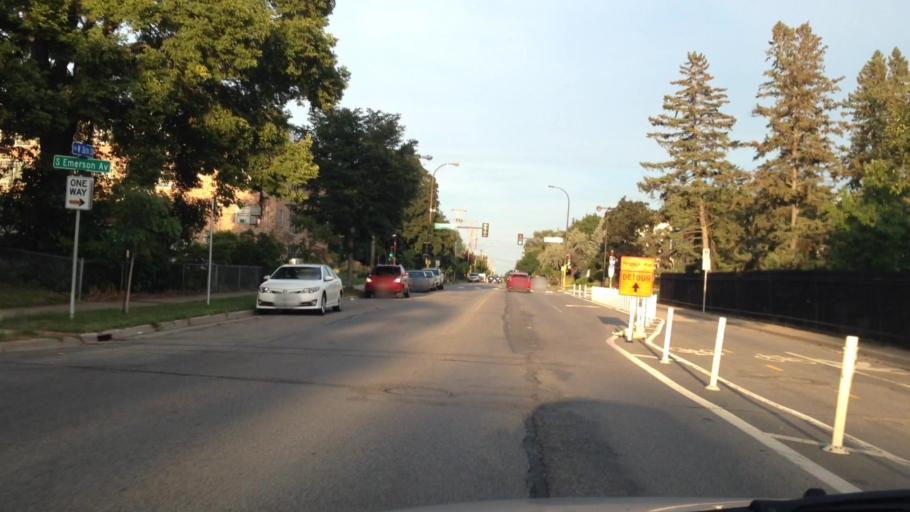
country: US
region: Minnesota
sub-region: Hennepin County
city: Minneapolis
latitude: 44.9377
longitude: -93.2947
